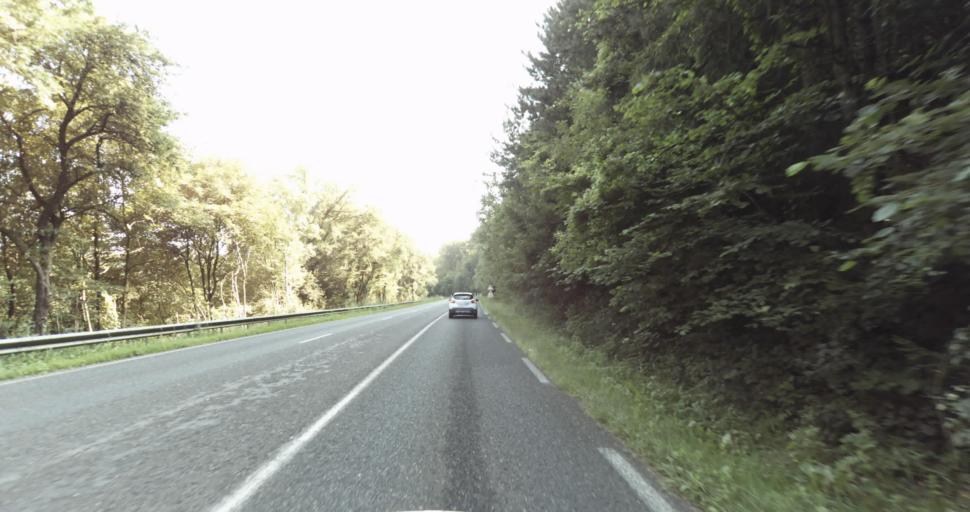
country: FR
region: Lorraine
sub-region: Departement de Meurthe-et-Moselle
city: Briey
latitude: 49.2660
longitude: 5.9257
